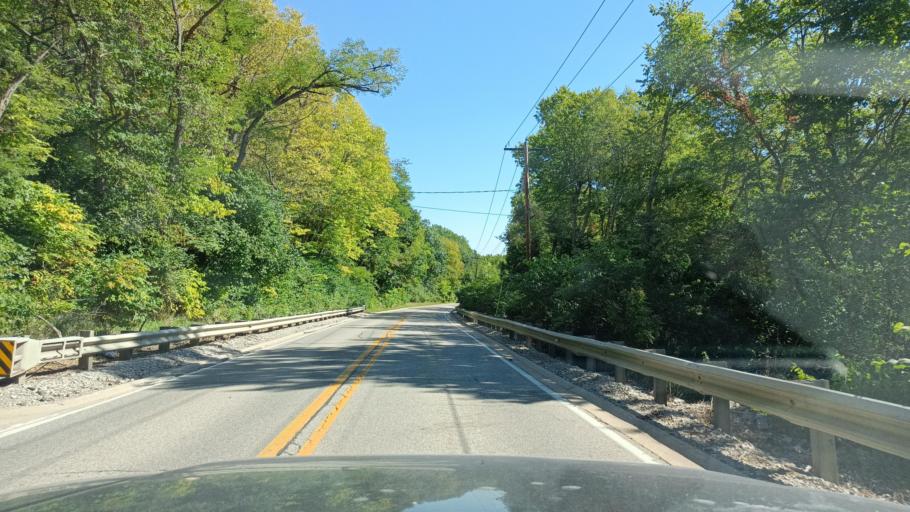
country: US
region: Illinois
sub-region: Woodford County
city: Eureka
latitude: 40.6272
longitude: -89.2505
